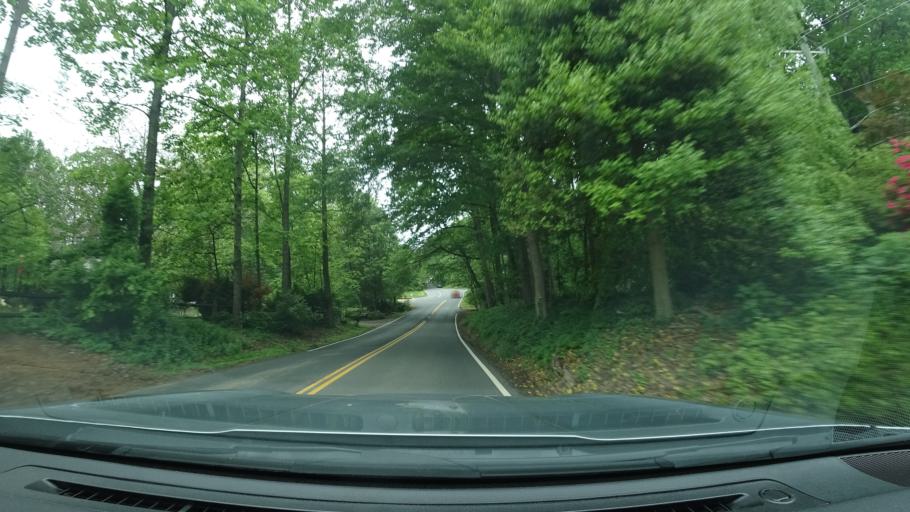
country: US
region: Virginia
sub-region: Fairfax County
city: Greenbriar
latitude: 38.8774
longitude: -77.3607
